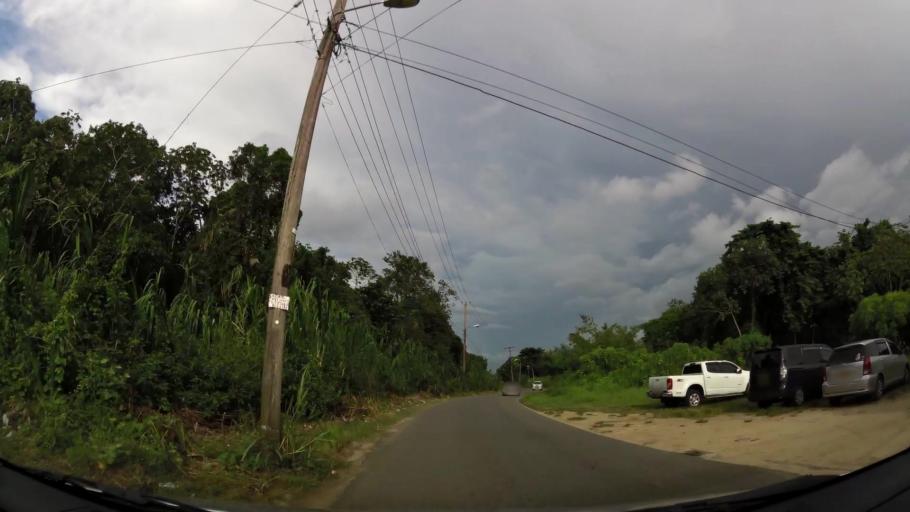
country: SR
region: Paramaribo
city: Paramaribo
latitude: 5.8459
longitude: -55.1764
